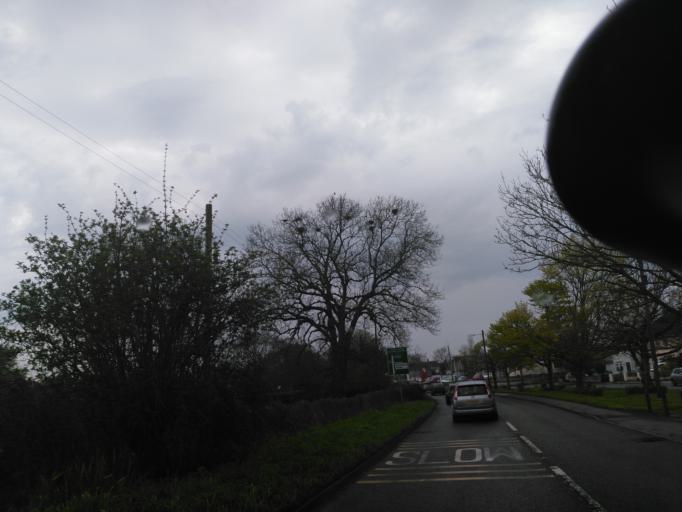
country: GB
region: England
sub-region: Somerset
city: Street
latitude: 51.1235
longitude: -2.7614
